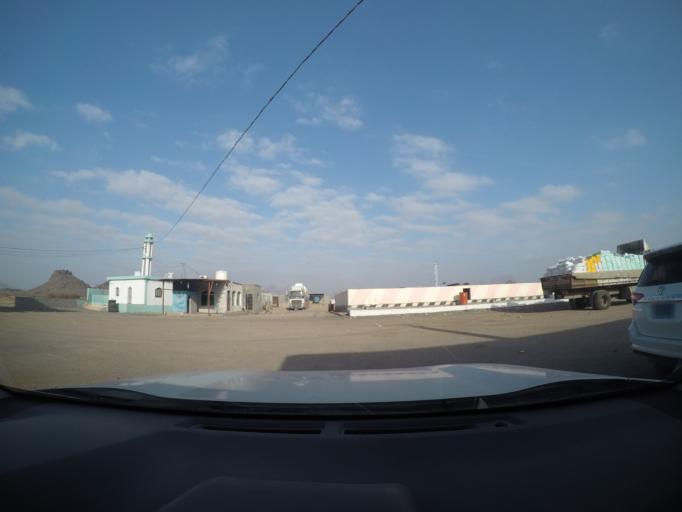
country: YE
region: Lahij
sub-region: Al Milah
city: Al Milah
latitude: 13.4116
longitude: 44.8127
